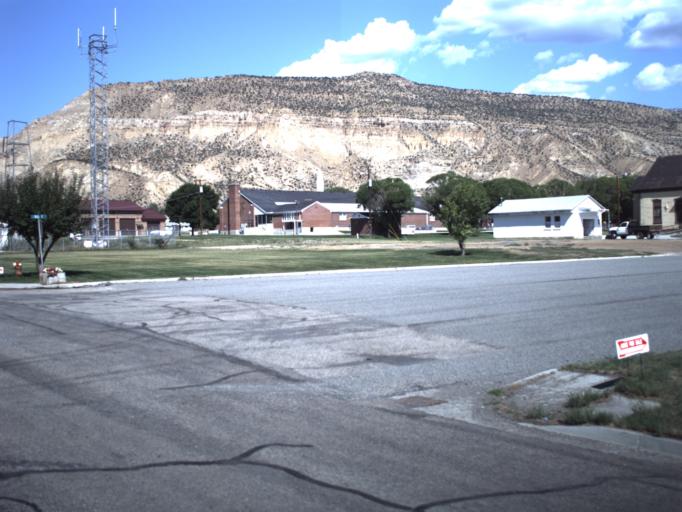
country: US
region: Utah
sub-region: Emery County
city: Ferron
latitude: 38.9232
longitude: -111.2465
